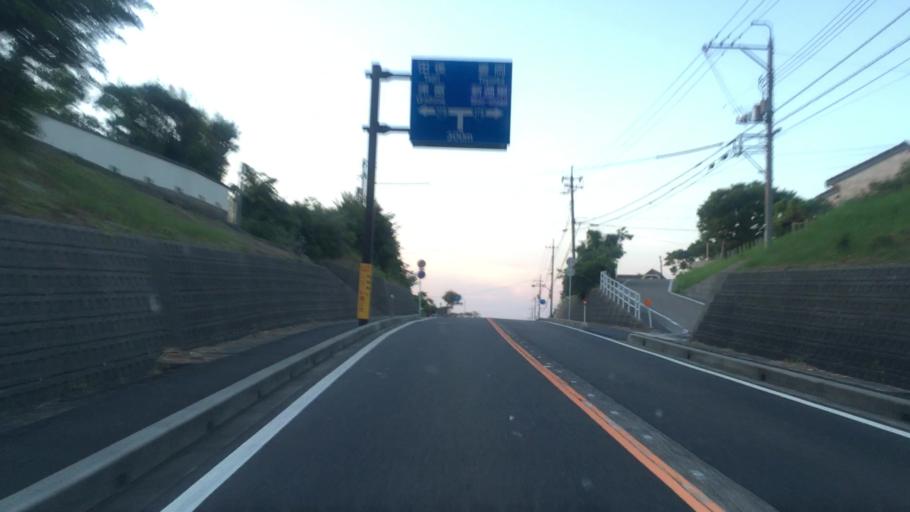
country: JP
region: Tottori
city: Tottori
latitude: 35.5879
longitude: 134.3325
